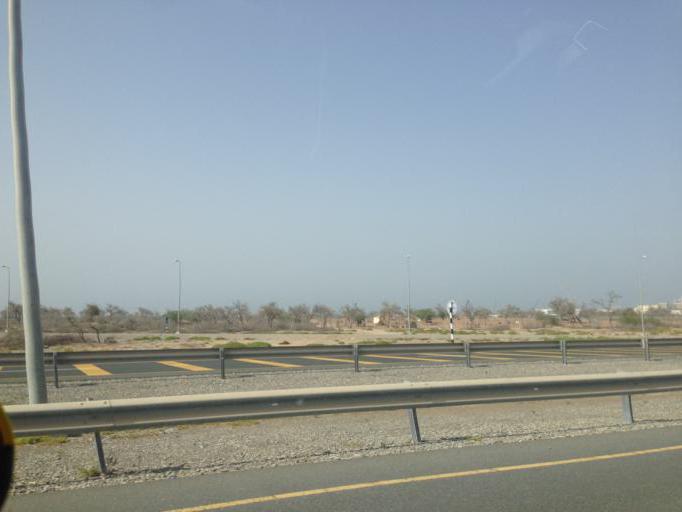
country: OM
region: Al Batinah
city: Barka'
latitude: 23.6974
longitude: 57.9642
